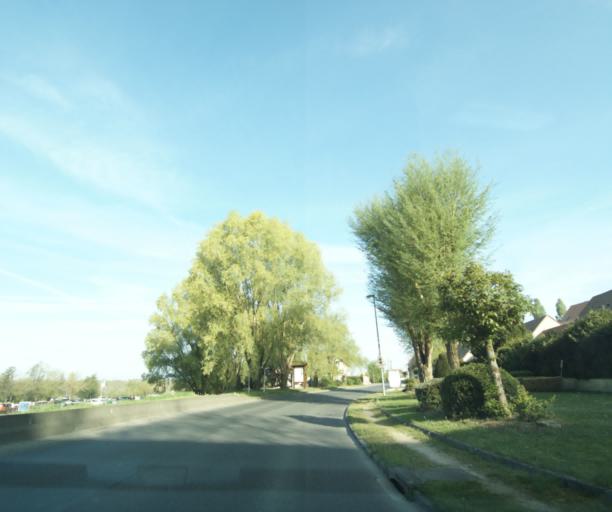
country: FR
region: Ile-de-France
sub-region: Departement de Seine-et-Marne
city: Saint-Mammes
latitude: 48.3809
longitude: 2.8126
